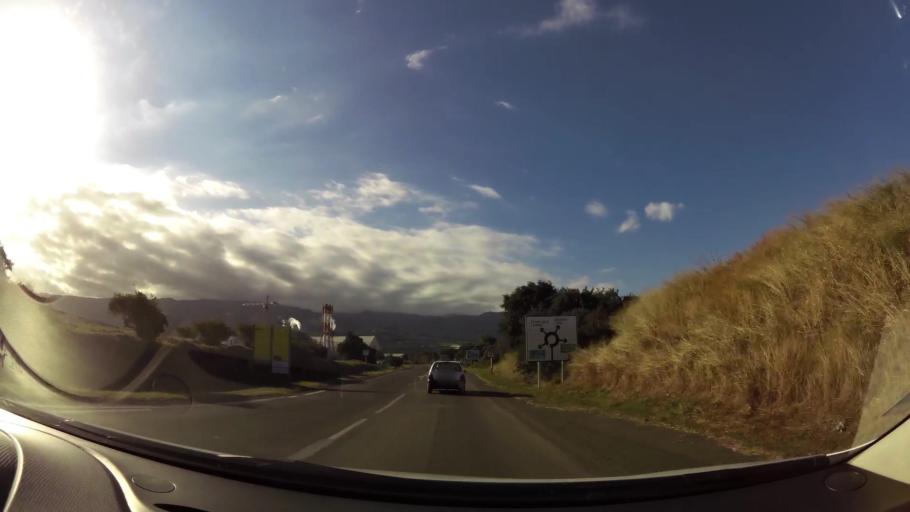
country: RE
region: Reunion
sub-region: Reunion
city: Saint-Louis
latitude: -21.2842
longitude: 55.3979
